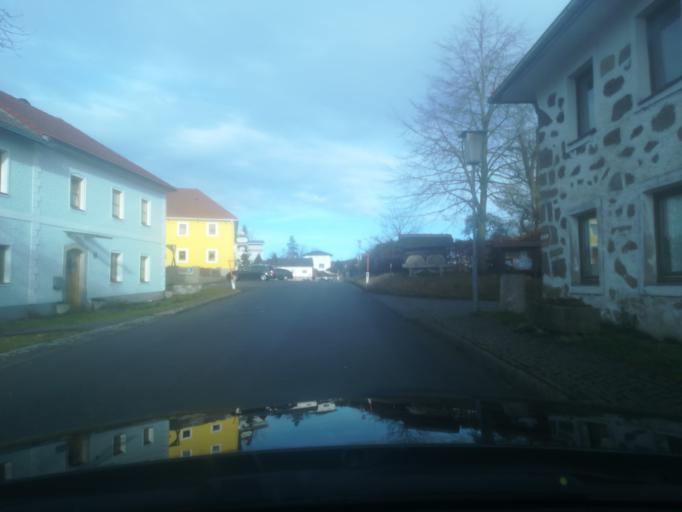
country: AT
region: Upper Austria
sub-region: Politischer Bezirk Perg
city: Perg
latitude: 48.3691
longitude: 14.6324
